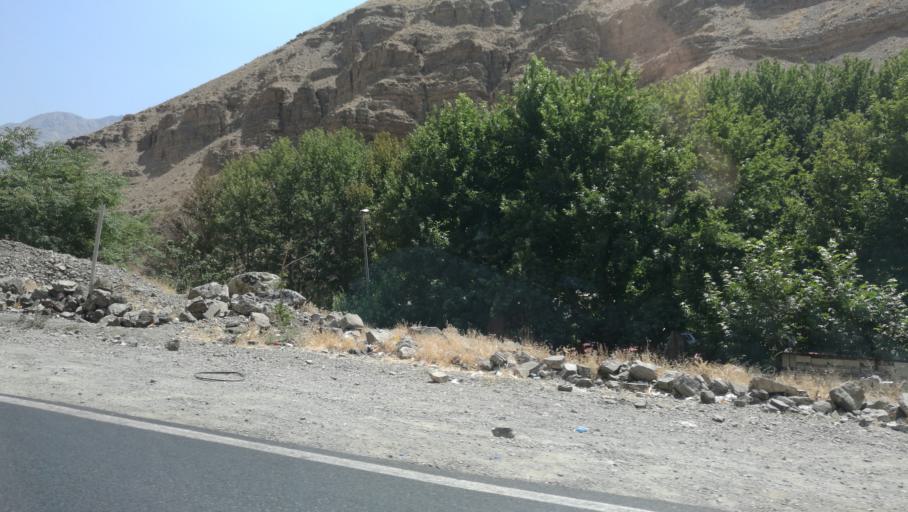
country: IR
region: Alborz
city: Karaj
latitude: 35.9471
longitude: 51.0706
